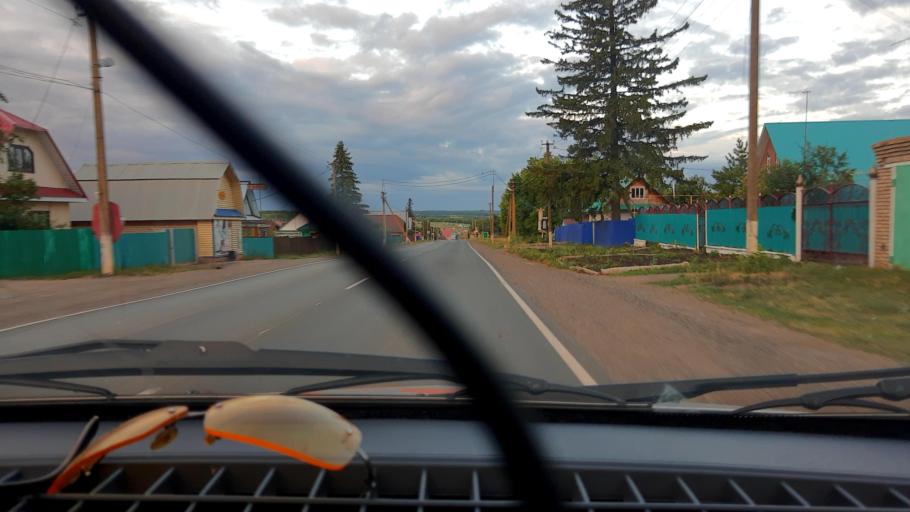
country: RU
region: Bashkortostan
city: Avdon
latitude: 54.5589
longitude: 55.6531
